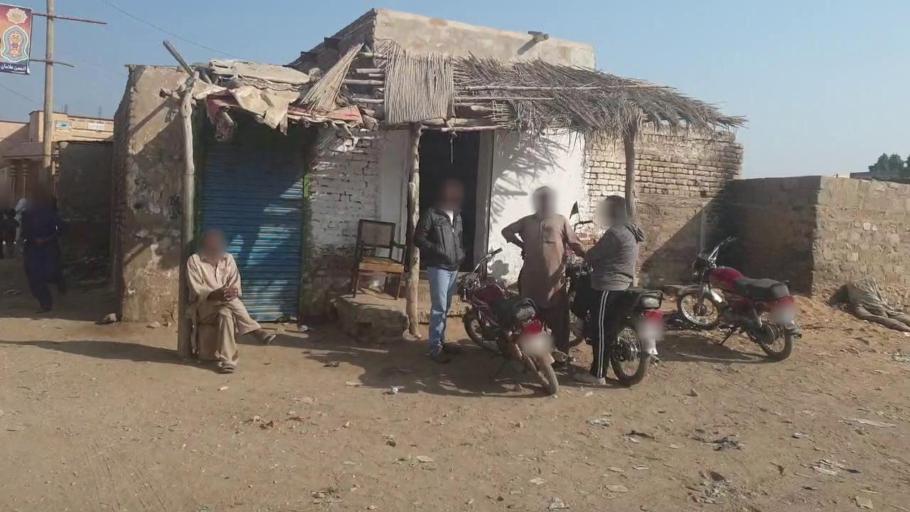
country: PK
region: Sindh
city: Kotri
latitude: 25.3671
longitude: 68.2869
